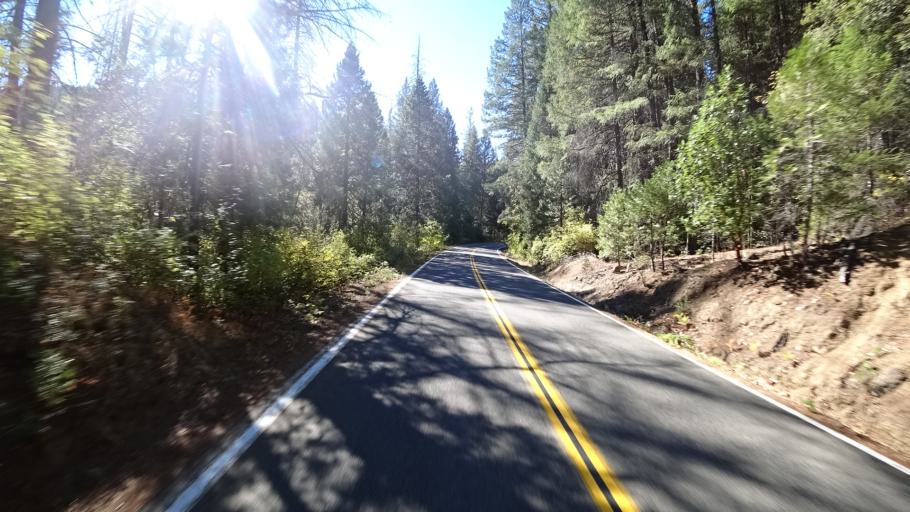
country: US
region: California
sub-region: Trinity County
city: Weaverville
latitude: 41.1869
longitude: -123.0771
